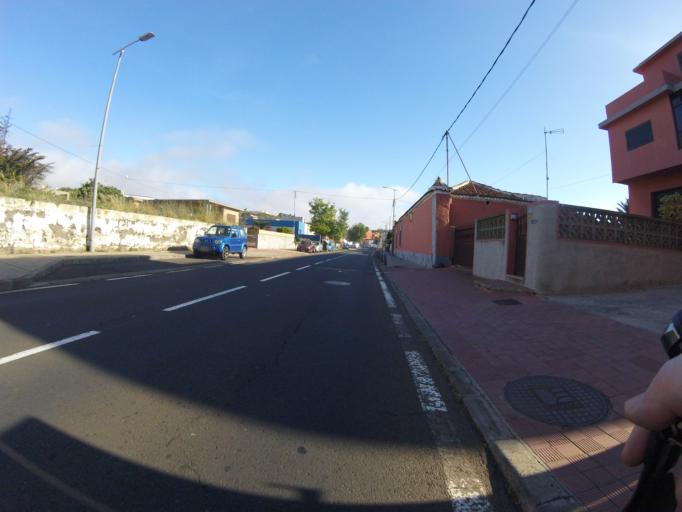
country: ES
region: Canary Islands
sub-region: Provincia de Santa Cruz de Tenerife
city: La Laguna
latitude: 28.4646
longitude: -16.3163
